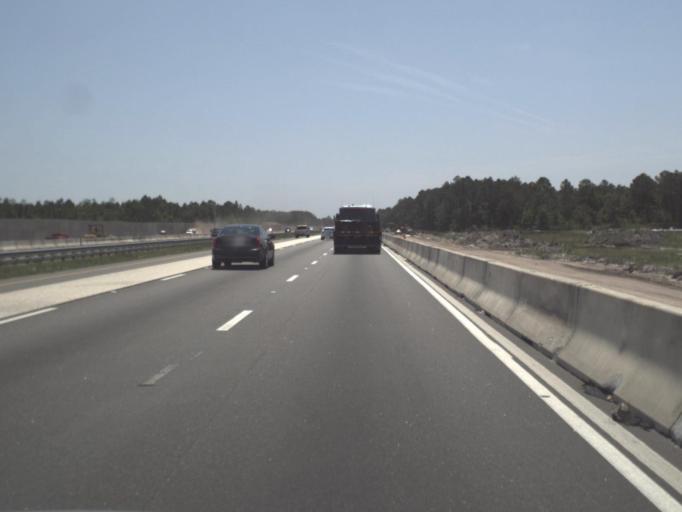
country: US
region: Florida
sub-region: Saint Johns County
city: Fruit Cove
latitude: 30.1109
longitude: -81.5107
